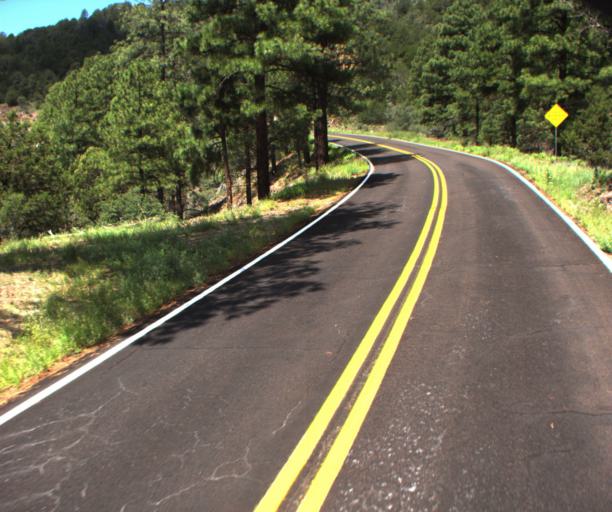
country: US
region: Arizona
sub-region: Greenlee County
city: Morenci
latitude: 33.4302
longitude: -109.3711
